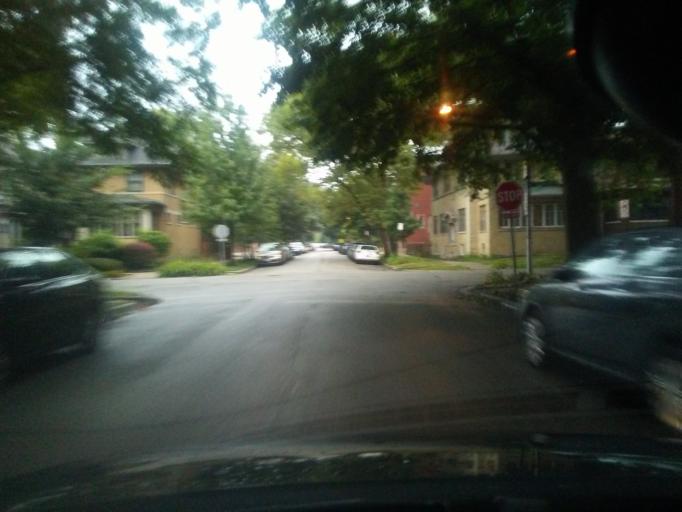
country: US
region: Illinois
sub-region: Cook County
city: Evanston
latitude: 41.9919
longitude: -87.6677
